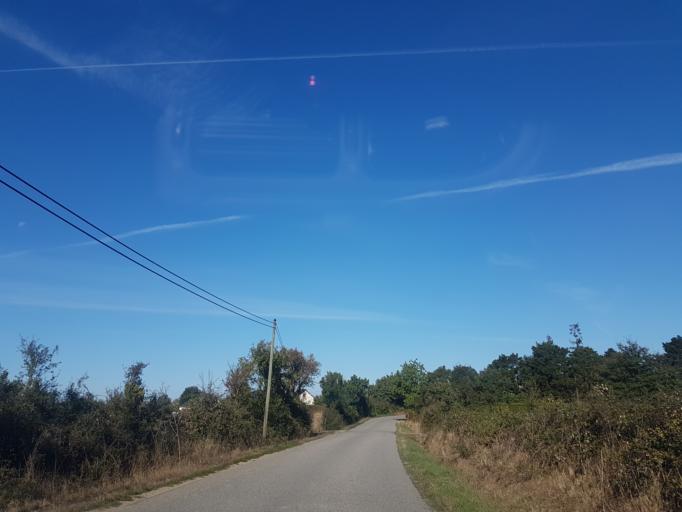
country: FR
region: Pays de la Loire
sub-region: Departement de la Loire-Atlantique
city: Petit-Mars
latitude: 47.3887
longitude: -1.4375
